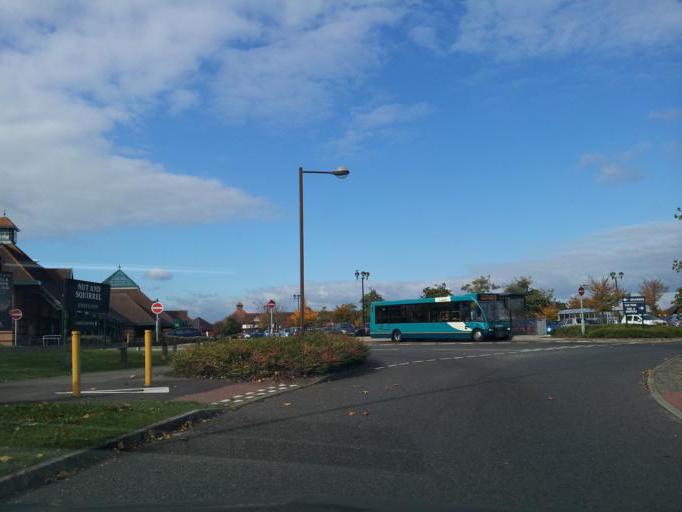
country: GB
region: England
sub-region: Milton Keynes
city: Shenley Church End
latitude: 52.0033
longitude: -0.7927
